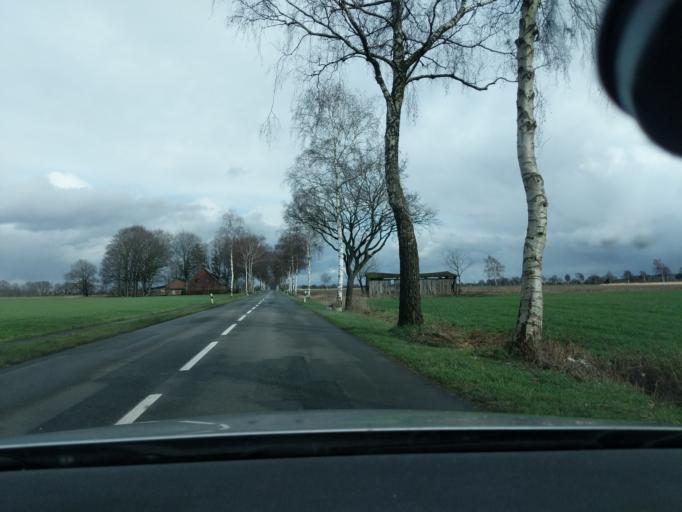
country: DE
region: Lower Saxony
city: Oldendorf
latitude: 53.5869
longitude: 9.2255
